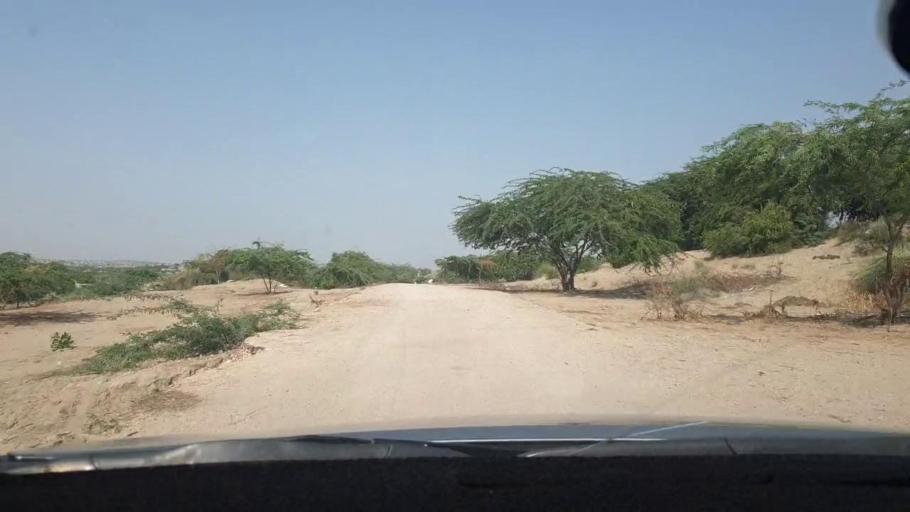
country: PK
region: Sindh
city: Pithoro
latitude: 25.7786
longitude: 69.4742
